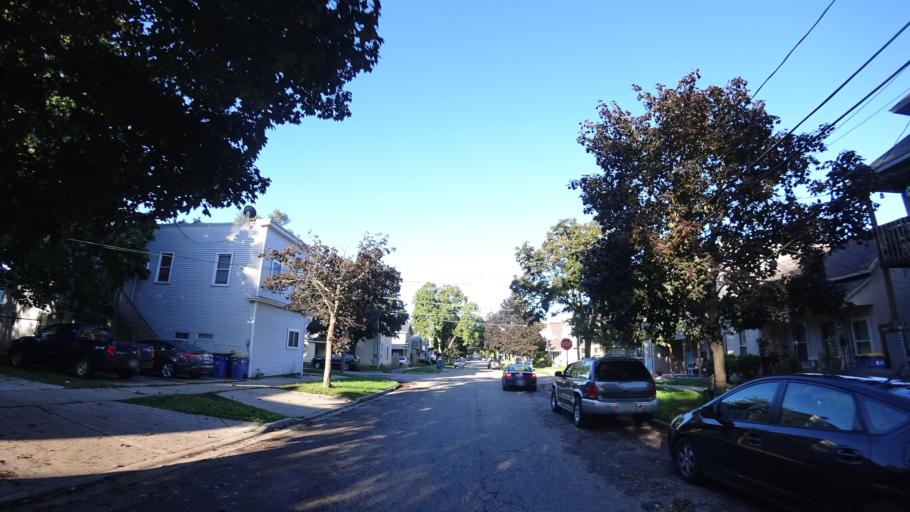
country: US
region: Michigan
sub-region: Kent County
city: Grand Rapids
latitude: 42.9618
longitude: -85.6907
